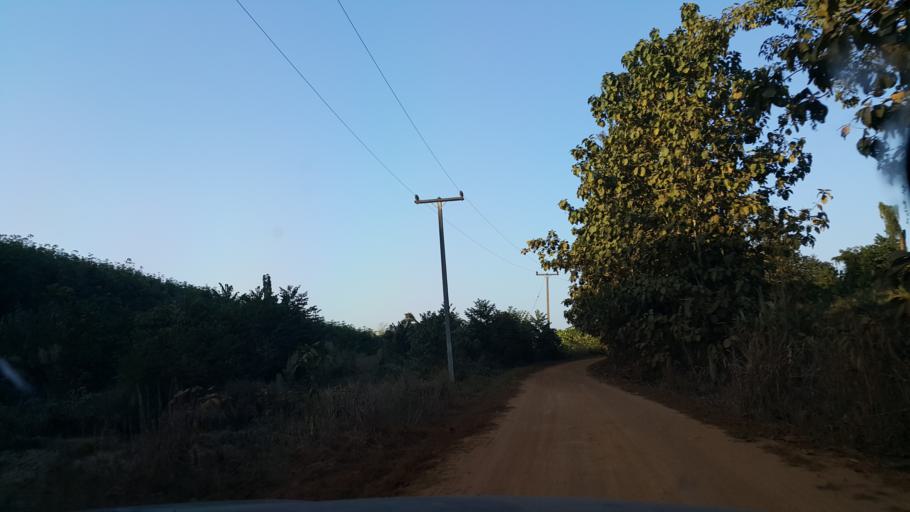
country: TH
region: Sukhothai
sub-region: Amphoe Si Satchanalai
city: Si Satchanalai
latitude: 17.6095
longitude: 99.6196
